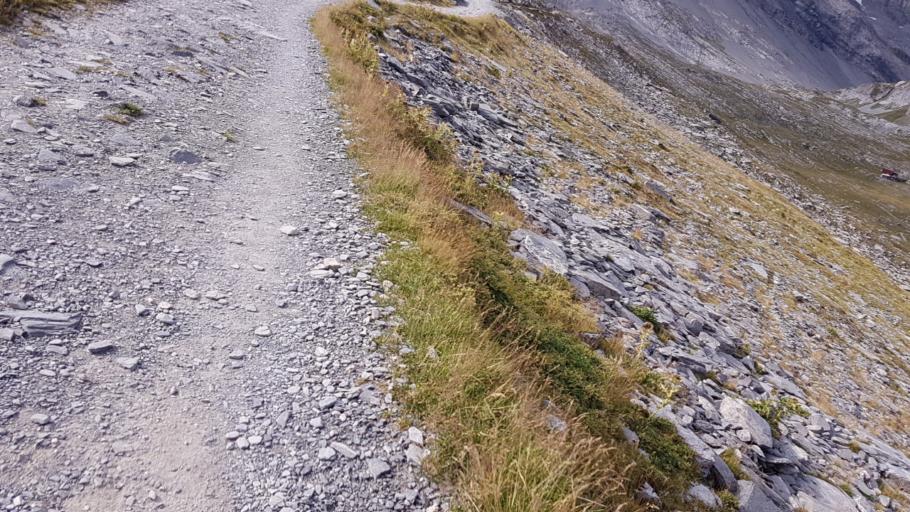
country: CH
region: Valais
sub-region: Leuk District
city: Leukerbad
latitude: 46.4063
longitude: 7.6215
